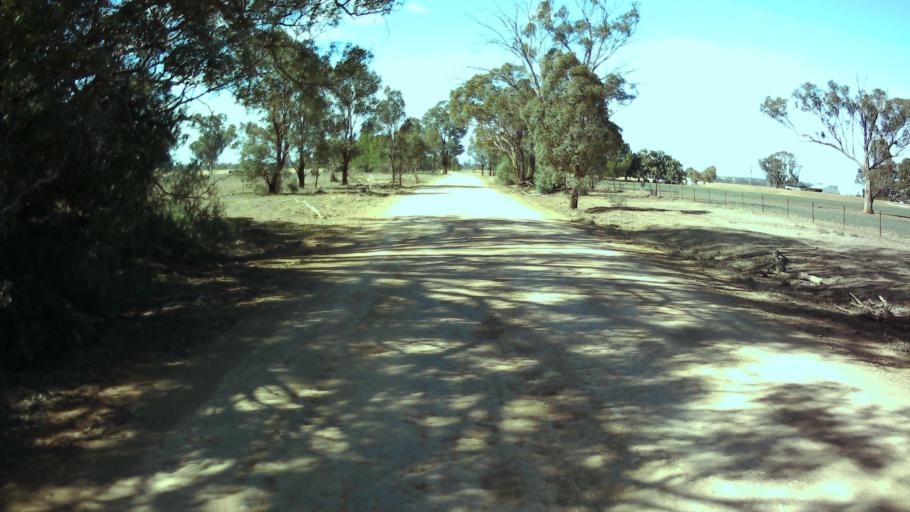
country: AU
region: New South Wales
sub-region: Weddin
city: Grenfell
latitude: -34.0274
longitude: 148.3179
